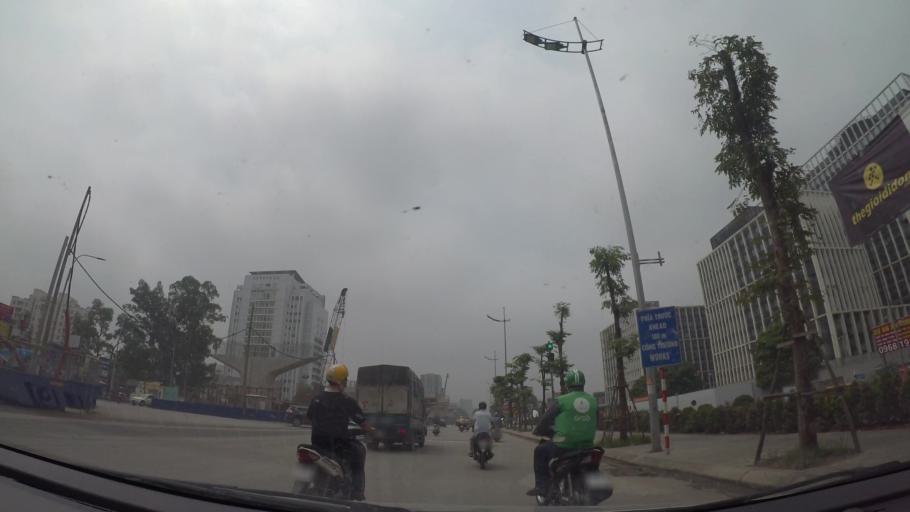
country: VN
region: Ha Noi
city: Cau Dien
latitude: 21.0492
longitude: 105.7813
